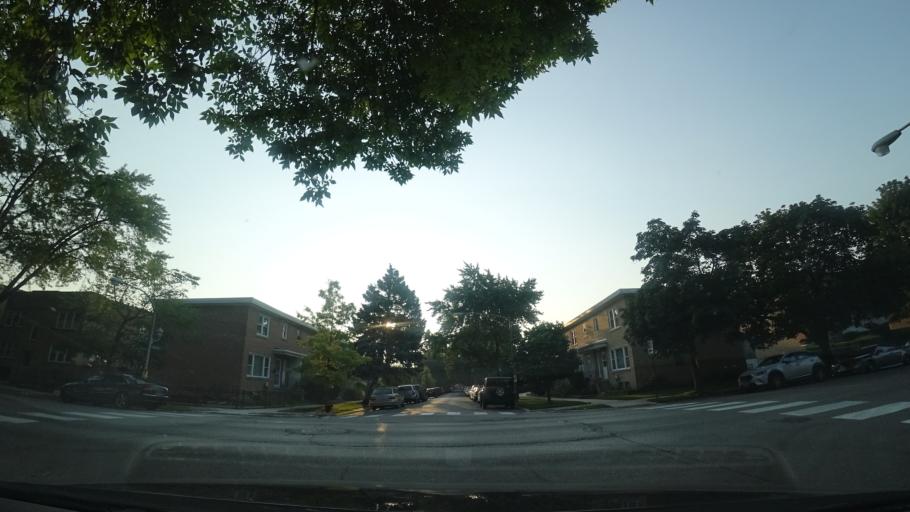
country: US
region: Illinois
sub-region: Cook County
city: Lincolnwood
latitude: 41.9804
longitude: -87.6992
